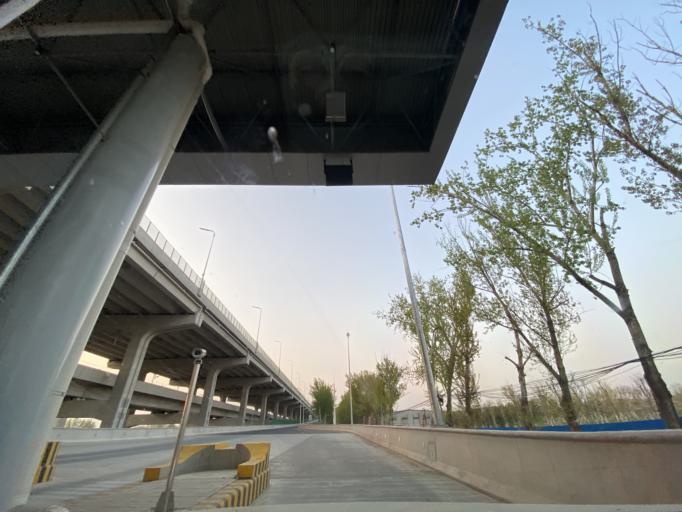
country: CN
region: Beijing
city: Weishanzhuang
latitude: 39.6161
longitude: 116.3790
